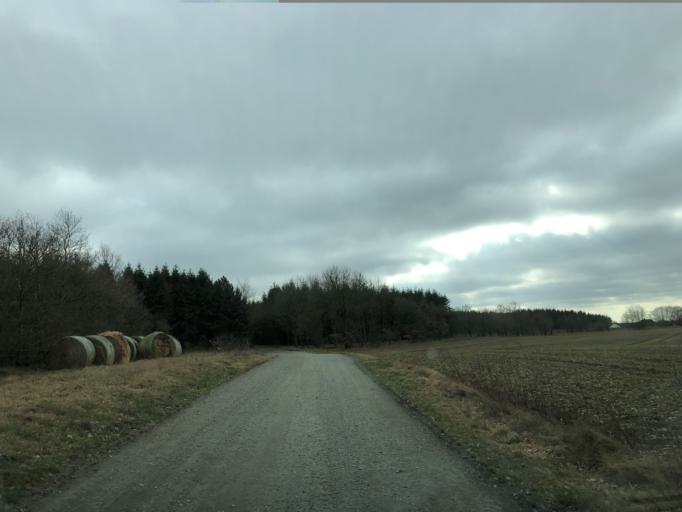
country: DK
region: South Denmark
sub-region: Billund Kommune
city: Billund
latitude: 55.7811
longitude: 9.1764
